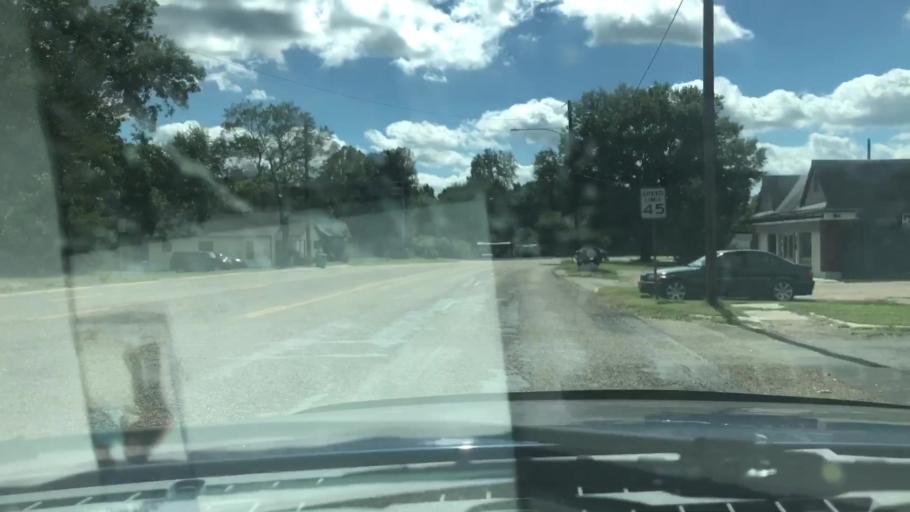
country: US
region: Texas
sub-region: Bowie County
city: Texarkana
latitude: 33.4072
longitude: -94.0607
